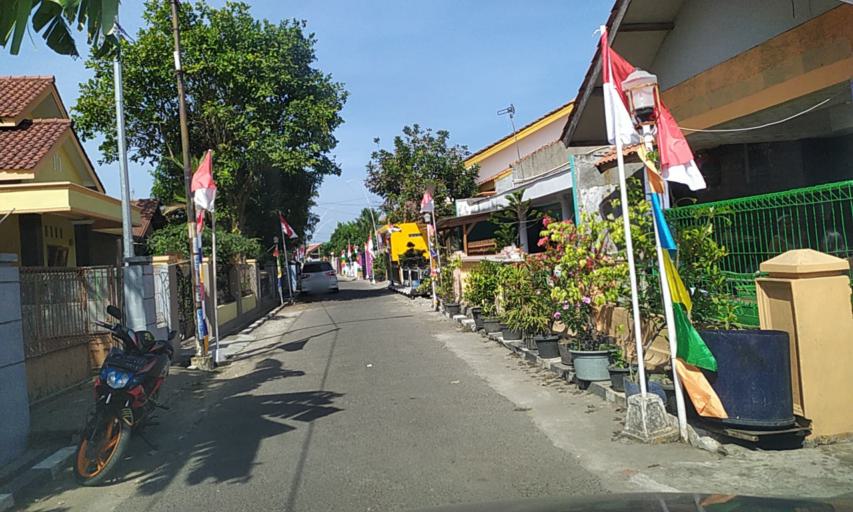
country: ID
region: Central Java
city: Karangbadar Kidul
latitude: -7.7153
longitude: 109.0090
